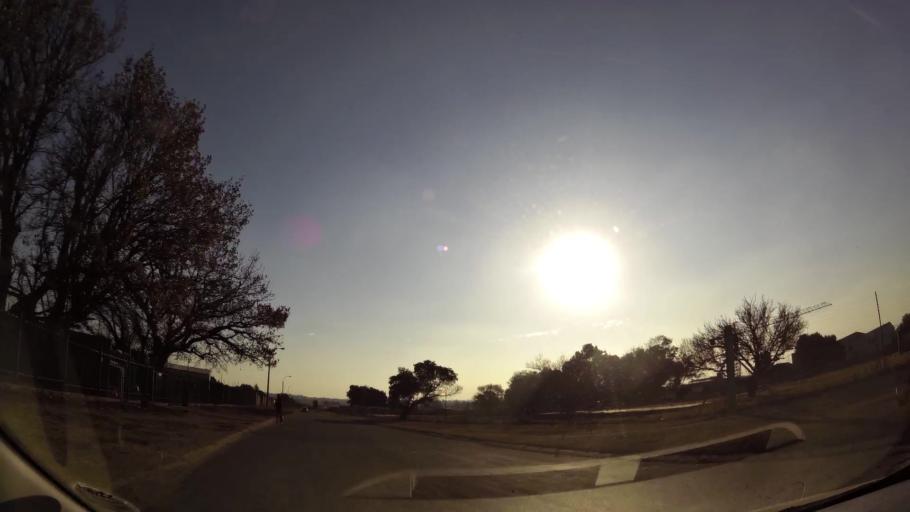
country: ZA
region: Gauteng
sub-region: West Rand District Municipality
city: Randfontein
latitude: -26.2025
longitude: 27.6883
